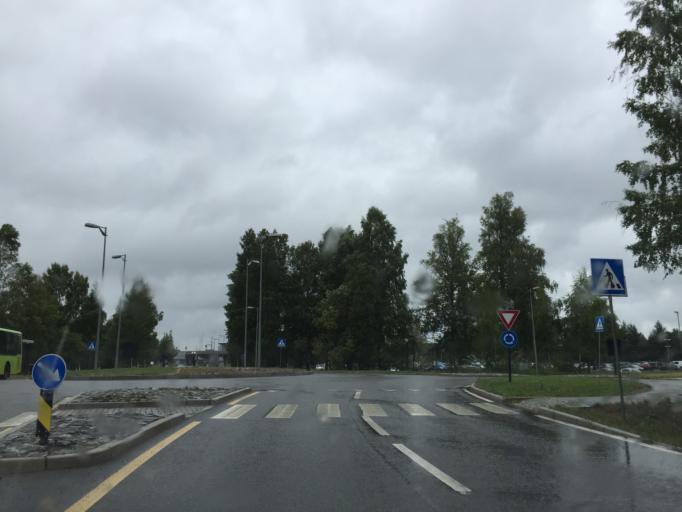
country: NO
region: Akershus
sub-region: Nannestad
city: Teigebyen
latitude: 60.1892
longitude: 11.0913
